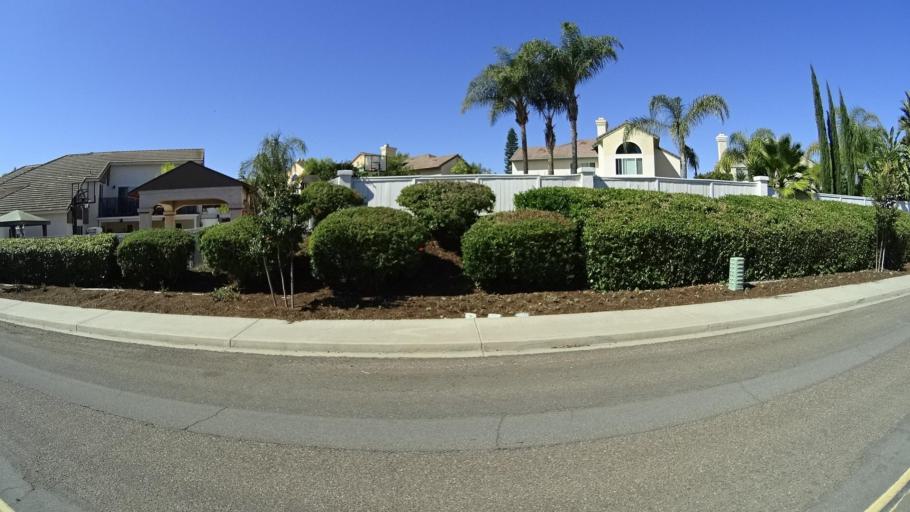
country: US
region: California
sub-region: San Diego County
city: Bonita
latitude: 32.6557
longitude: -116.9868
